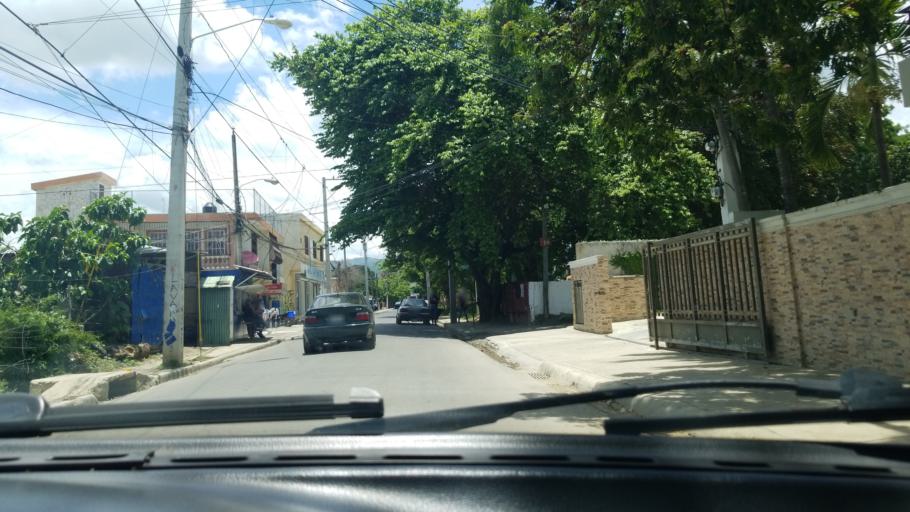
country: DO
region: Santiago
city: Santiago de los Caballeros
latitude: 19.4842
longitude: -70.6803
